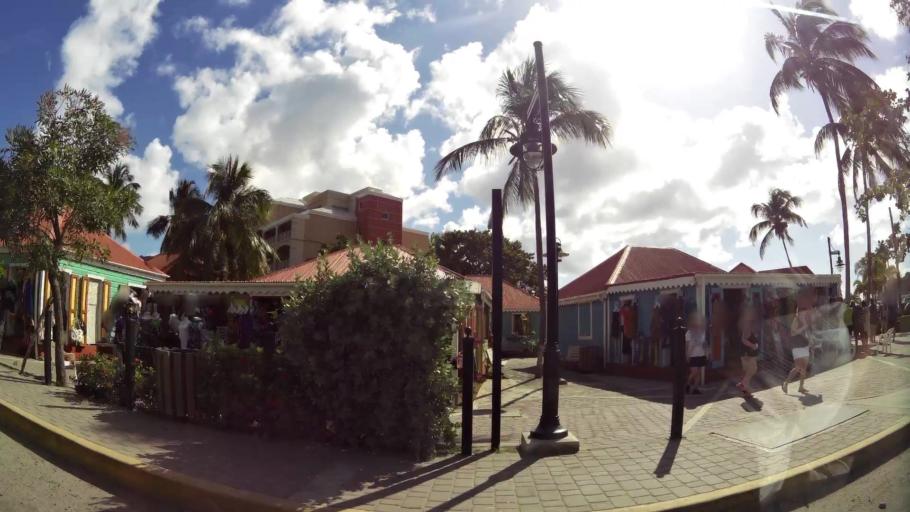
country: VG
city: Road Town
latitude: 18.4204
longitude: -64.6177
